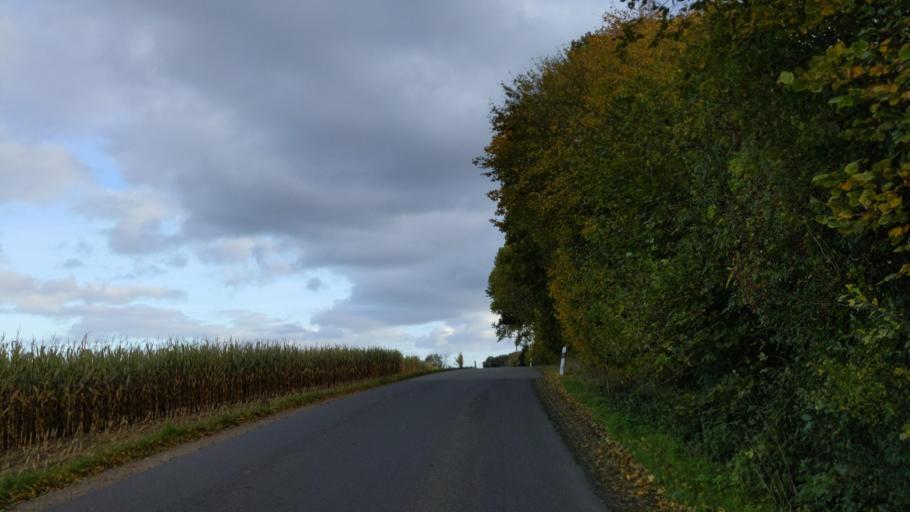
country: DE
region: Schleswig-Holstein
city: Susel
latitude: 54.1033
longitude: 10.7222
